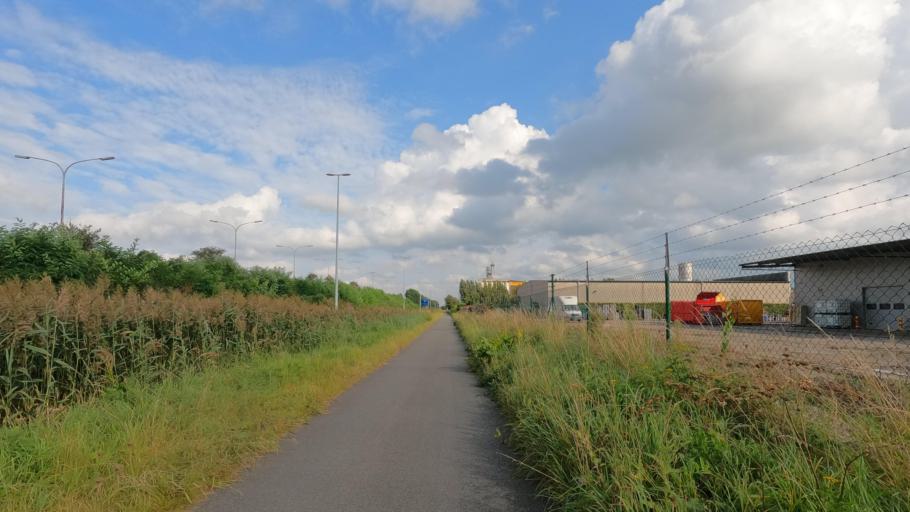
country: BE
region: Flanders
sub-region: Provincie Oost-Vlaanderen
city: Sint-Gillis-Waas
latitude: 51.2306
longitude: 4.0976
